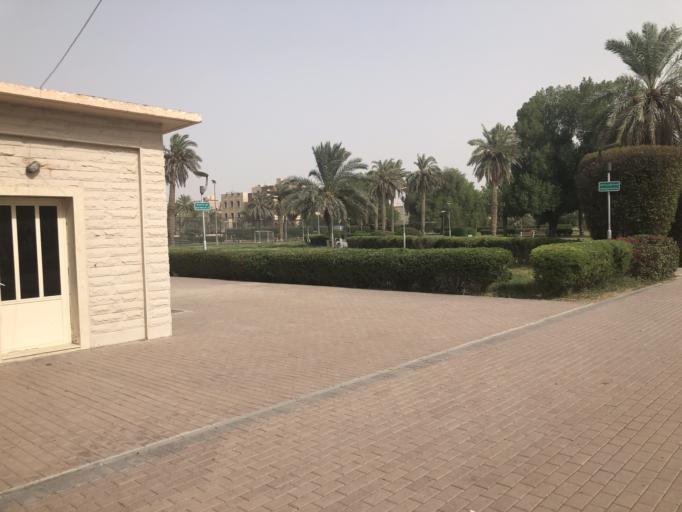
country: KW
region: Al Asimah
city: Ash Shamiyah
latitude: 29.3321
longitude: 47.9901
